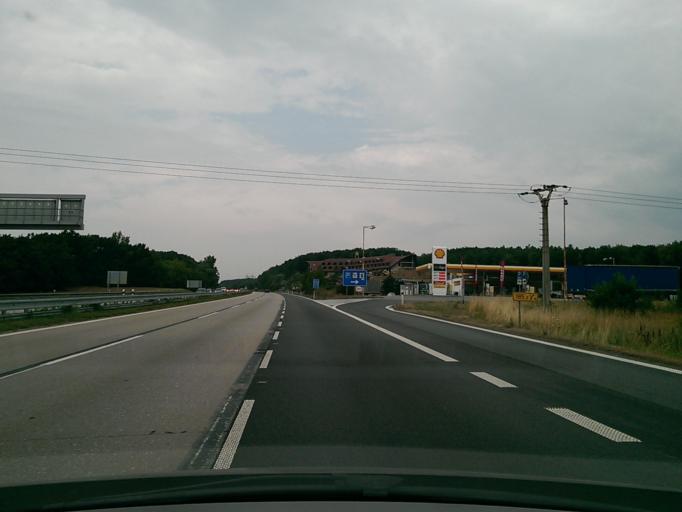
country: CZ
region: South Moravian
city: Troubsko
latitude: 49.1822
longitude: 16.4805
